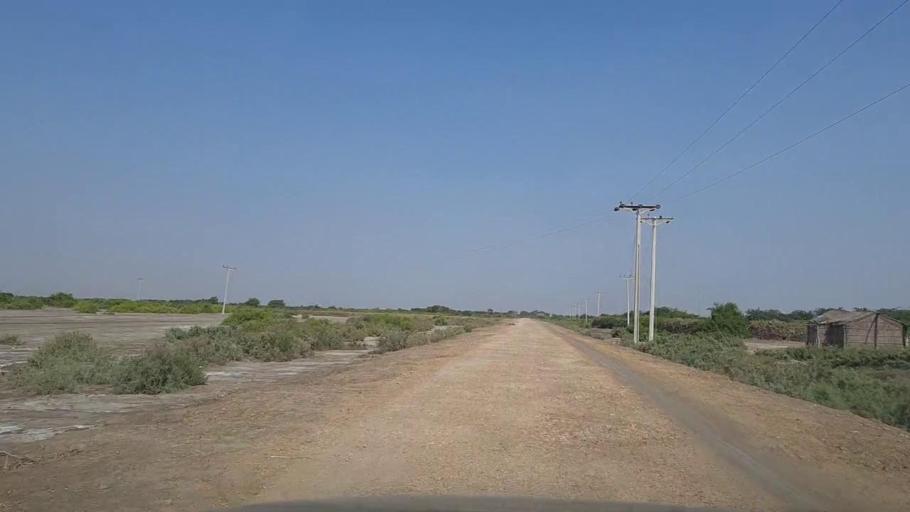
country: PK
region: Sindh
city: Thatta
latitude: 24.6061
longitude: 67.9547
